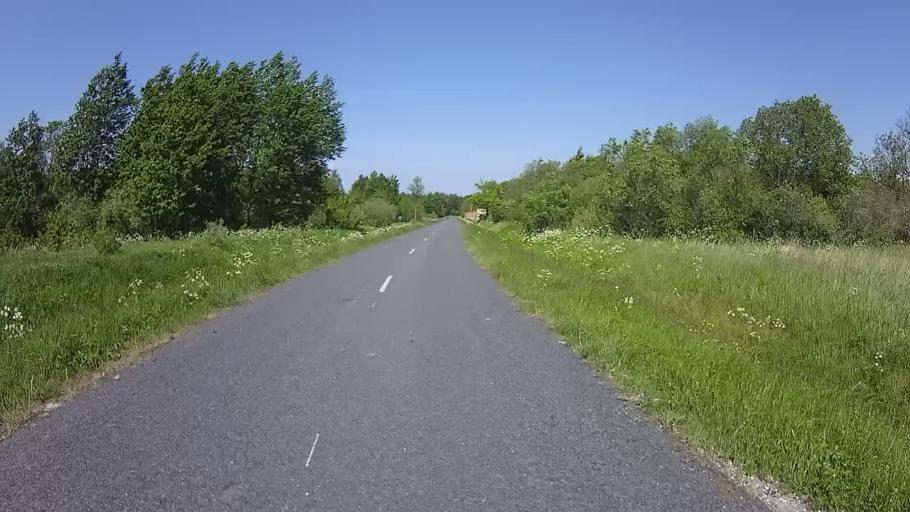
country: LV
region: Dundaga
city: Dundaga
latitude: 57.9374
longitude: 22.0918
